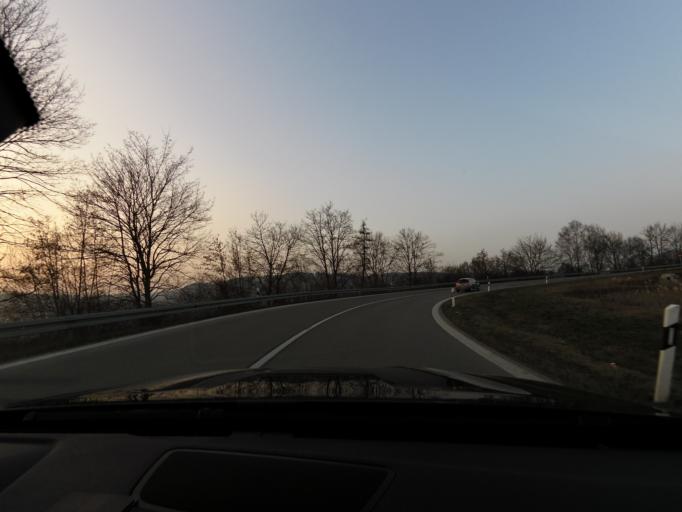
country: DE
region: Bavaria
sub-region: Lower Bavaria
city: Eching
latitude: 48.5335
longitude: 12.0703
